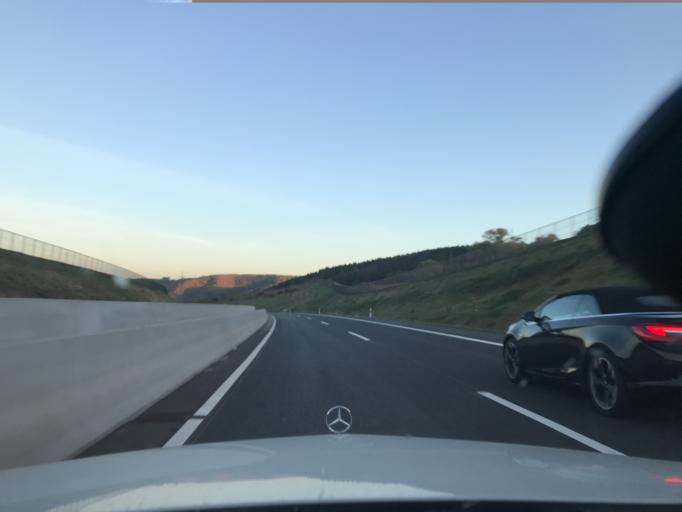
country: DE
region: Hesse
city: Waldkappel
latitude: 51.1582
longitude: 9.8544
